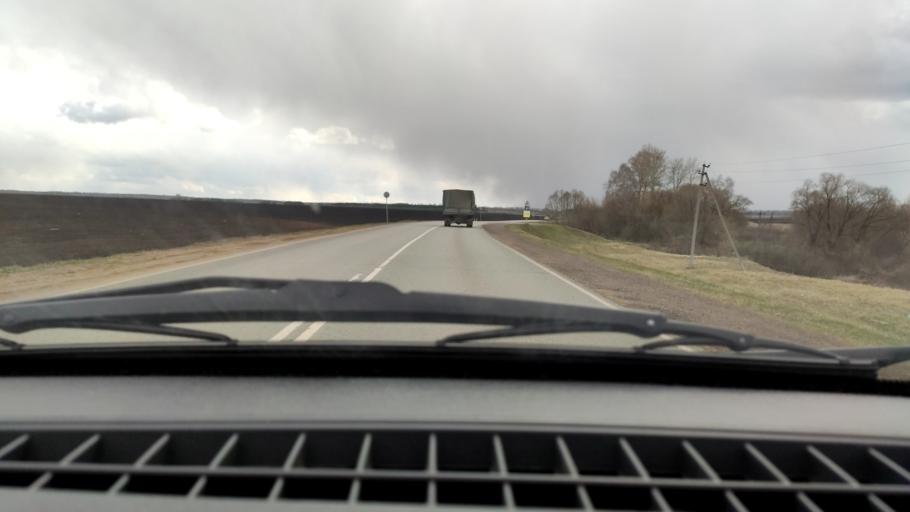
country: RU
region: Bashkortostan
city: Kushnarenkovo
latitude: 55.0686
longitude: 55.2584
